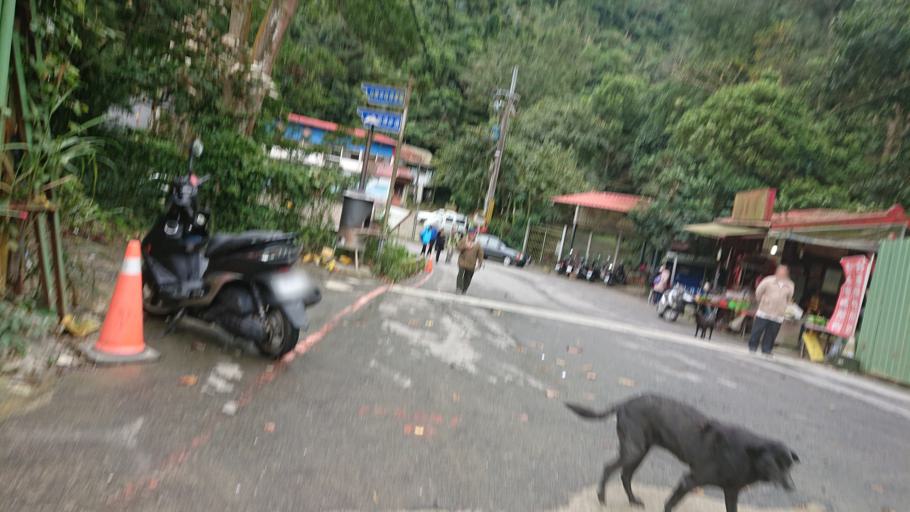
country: TW
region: Taipei
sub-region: Taipei
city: Banqiao
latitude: 24.9496
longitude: 121.4493
